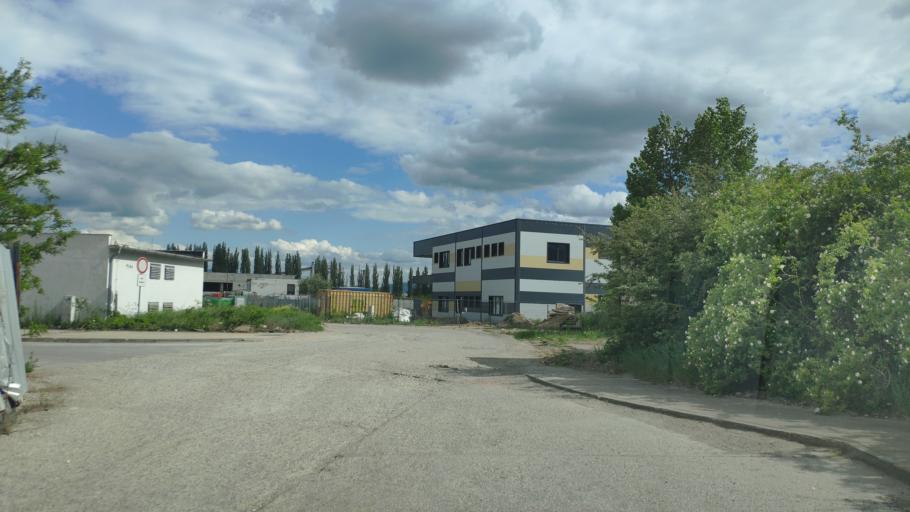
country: SK
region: Kosicky
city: Kosice
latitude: 48.6801
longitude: 21.2877
